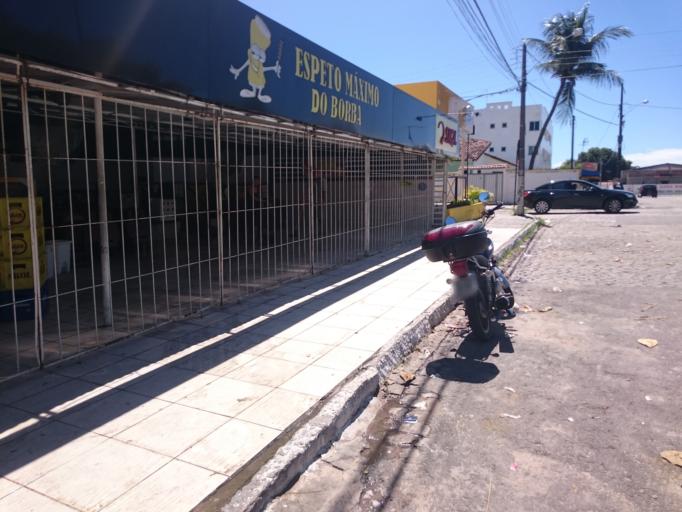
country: BR
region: Paraiba
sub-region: Joao Pessoa
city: Joao Pessoa
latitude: -7.1475
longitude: -34.8444
